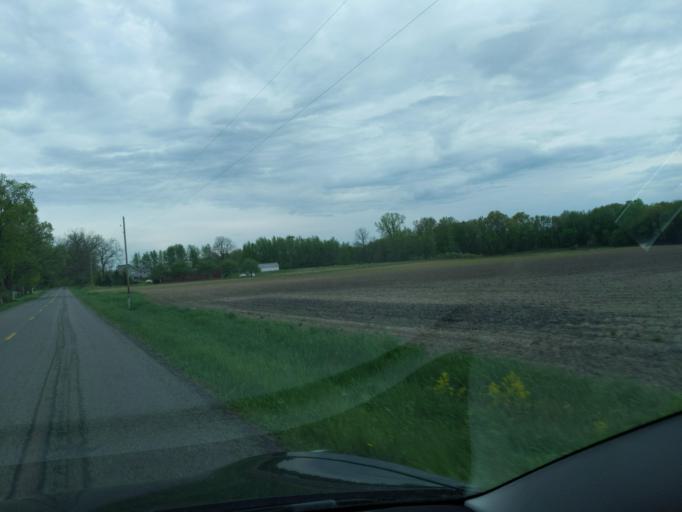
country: US
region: Michigan
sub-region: Ingham County
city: Stockbridge
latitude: 42.4345
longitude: -84.2584
